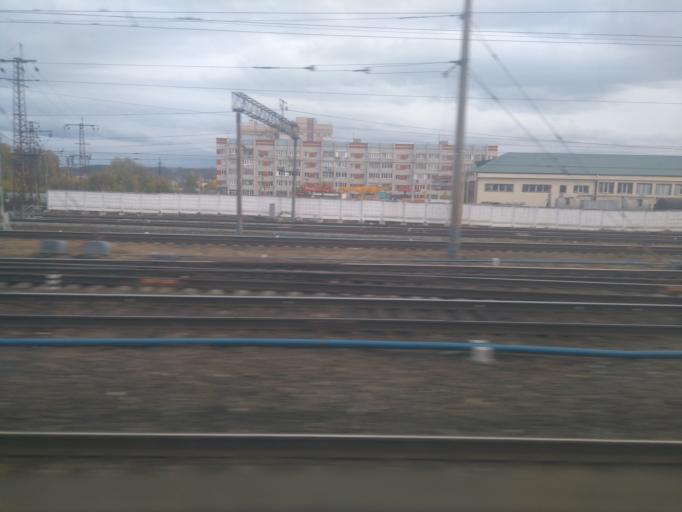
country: RU
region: Tatarstan
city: Staroye Arakchino
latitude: 55.8160
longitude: 48.9094
